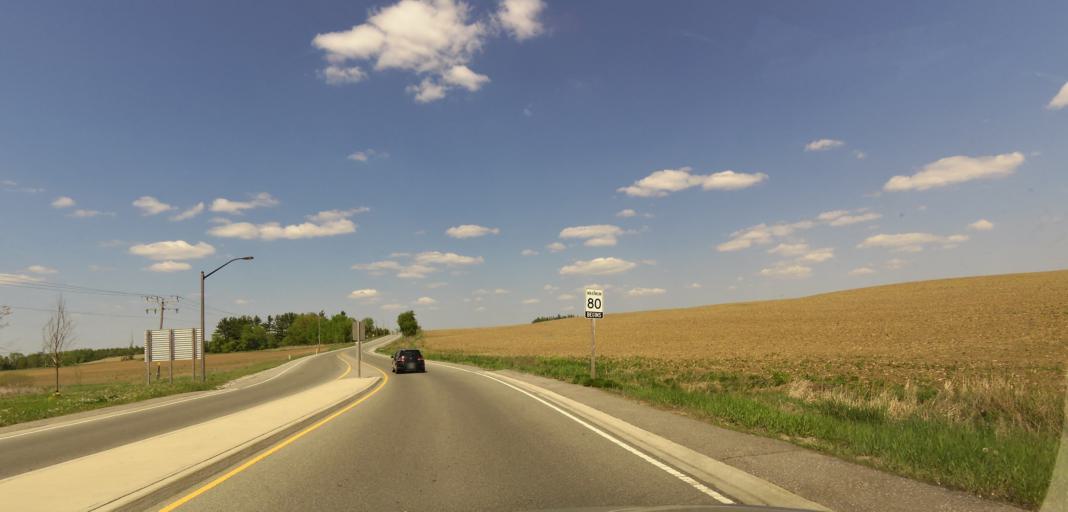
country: CA
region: Ontario
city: Brampton
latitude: 43.8300
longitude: -79.8829
